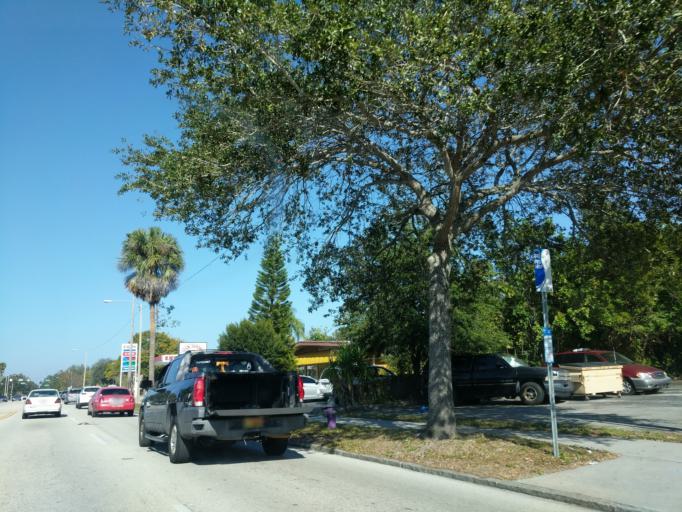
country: US
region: Florida
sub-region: Pinellas County
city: Lealman
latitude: 27.8010
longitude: -82.6468
